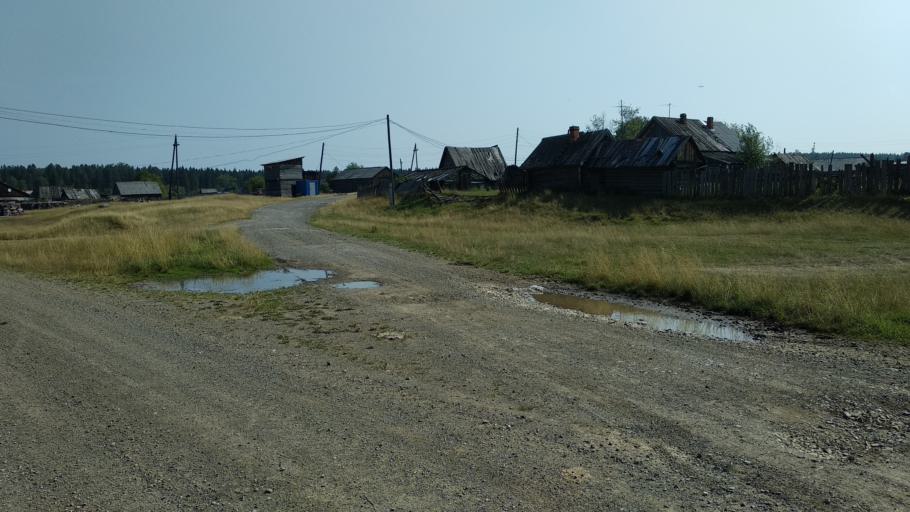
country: RU
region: Sverdlovsk
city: Karpinsk
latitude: 59.4484
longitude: 60.0112
